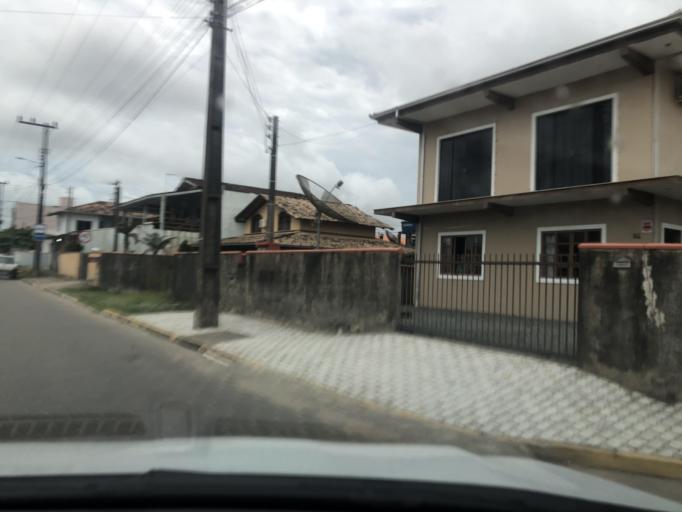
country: BR
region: Santa Catarina
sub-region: Sao Francisco Do Sul
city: Sao Francisco do Sul
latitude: -26.2264
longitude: -48.5253
